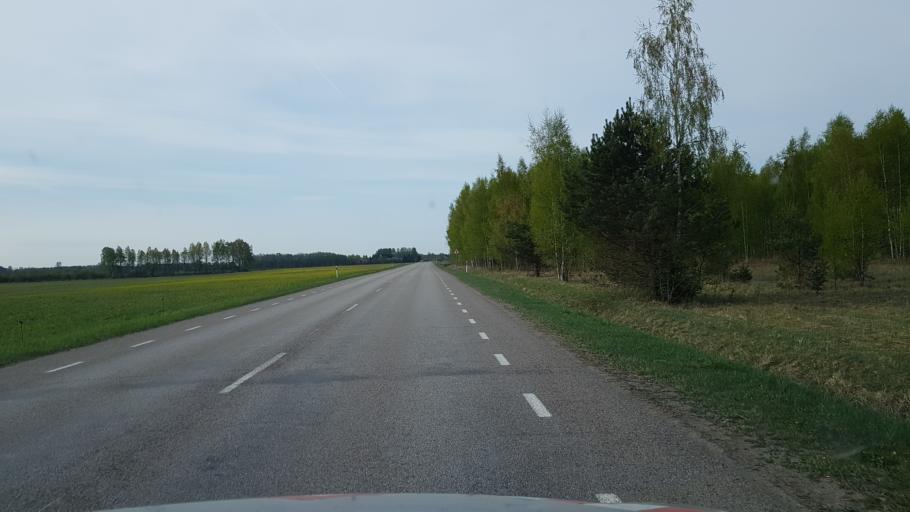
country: EE
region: Paernumaa
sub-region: Audru vald
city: Audru
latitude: 58.3834
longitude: 24.2723
